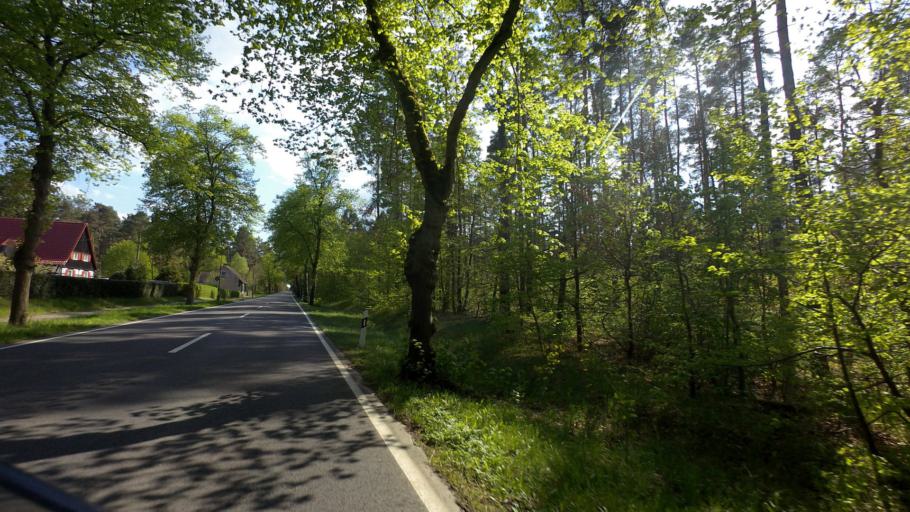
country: DE
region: Brandenburg
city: Milmersdorf
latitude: 53.0417
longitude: 13.6033
